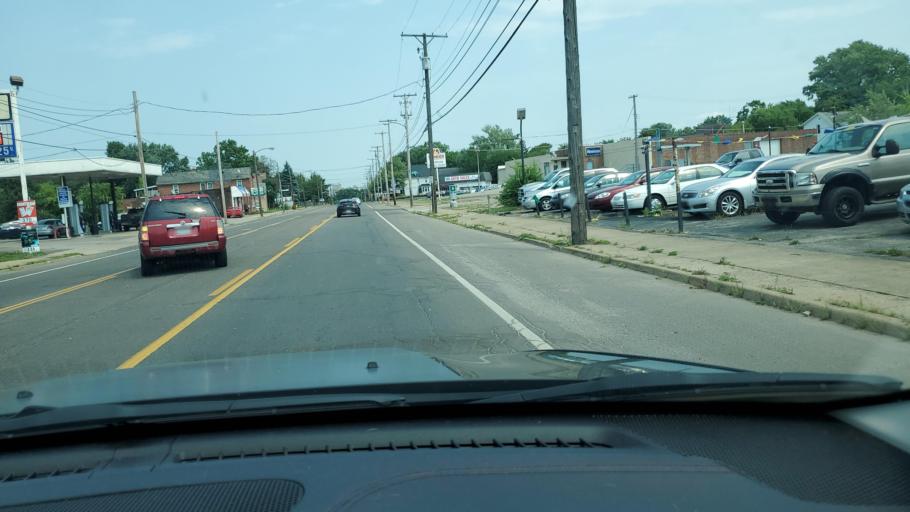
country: US
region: Ohio
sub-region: Mahoning County
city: Youngstown
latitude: 41.1019
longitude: -80.6811
